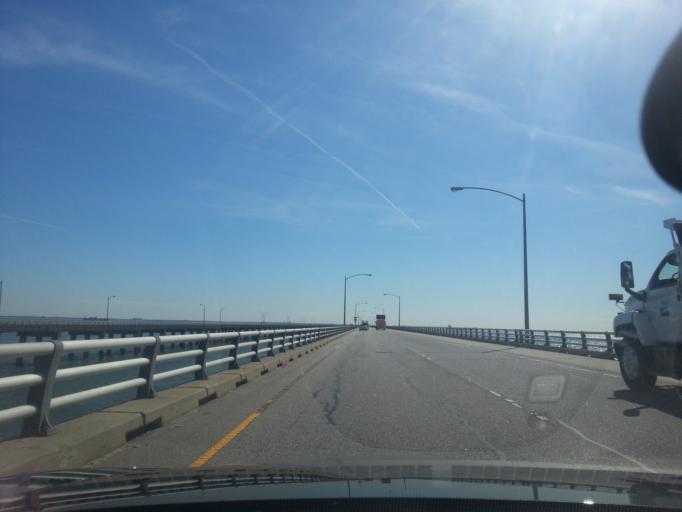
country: US
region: Virginia
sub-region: City of Virginia Beach
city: Virginia Beach
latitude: 37.0092
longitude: -76.0957
